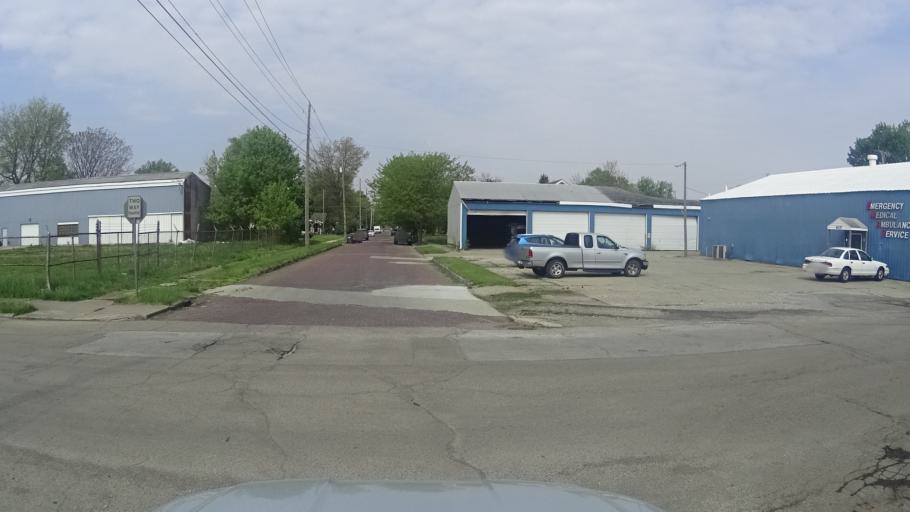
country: US
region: Indiana
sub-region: Madison County
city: Anderson
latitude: 40.1089
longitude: -85.6872
